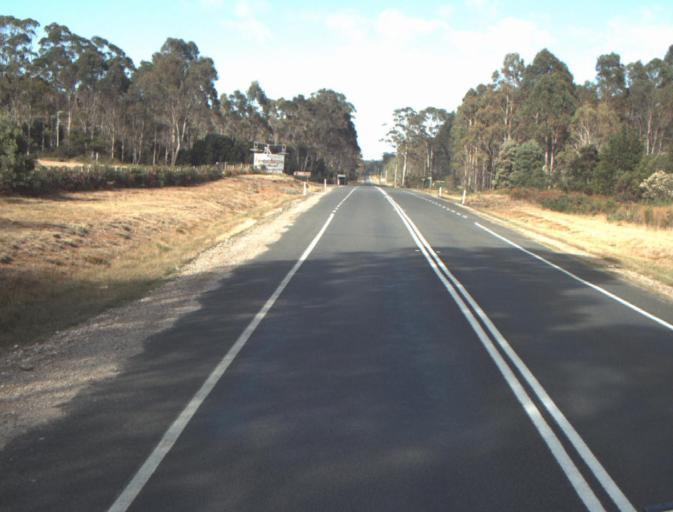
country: AU
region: Tasmania
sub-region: Launceston
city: Mayfield
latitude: -41.3110
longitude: 147.2004
